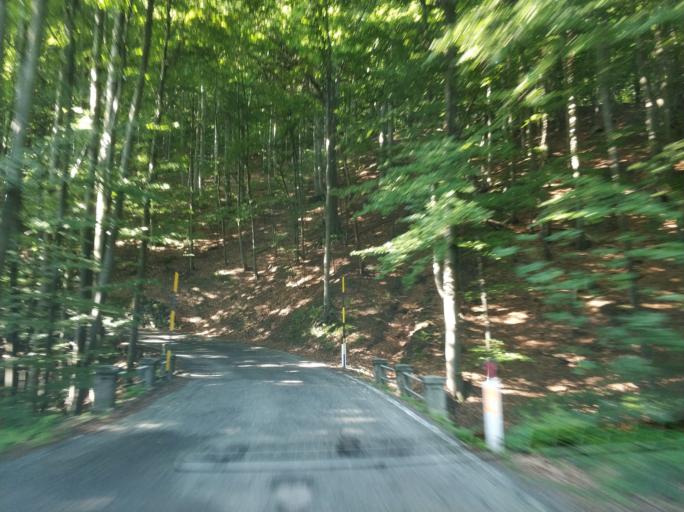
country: IT
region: Piedmont
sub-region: Provincia di Torino
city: Viu
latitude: 45.2006
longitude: 7.3673
